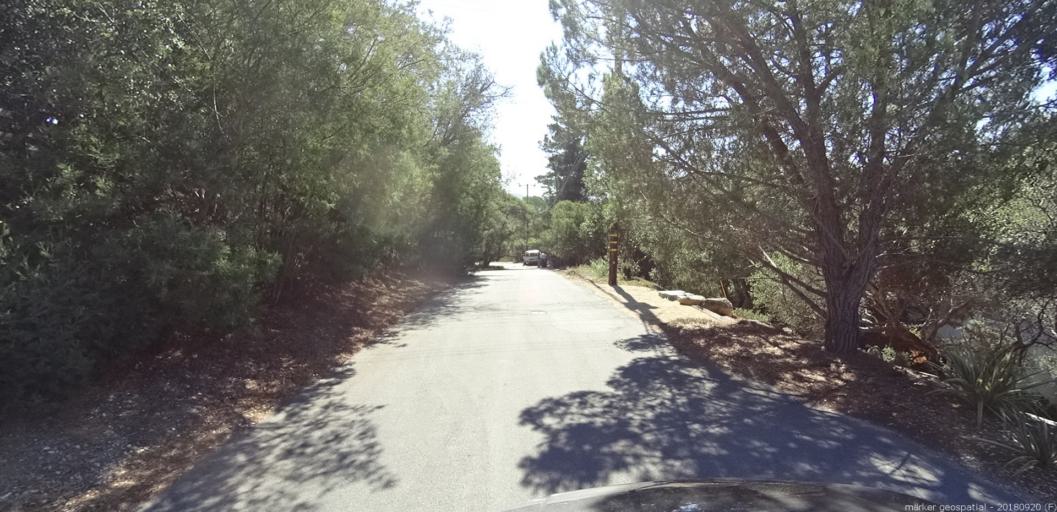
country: US
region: California
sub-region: Monterey County
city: Carmel-by-the-Sea
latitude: 36.5499
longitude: -121.8985
